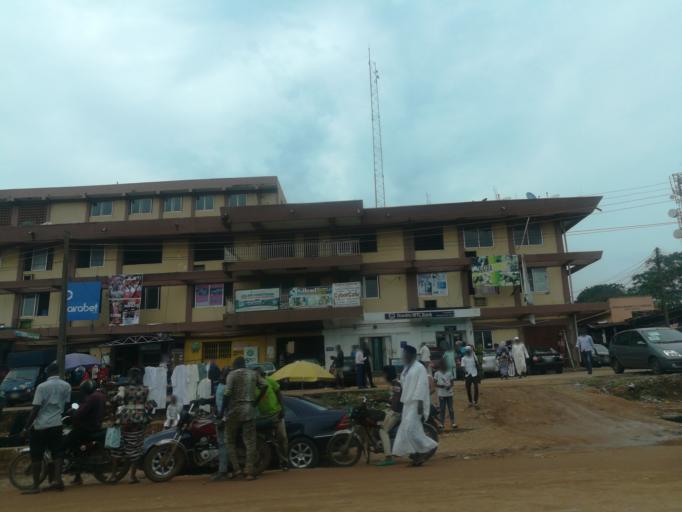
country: NG
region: Oyo
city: Ibadan
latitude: 7.3978
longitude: 3.9201
